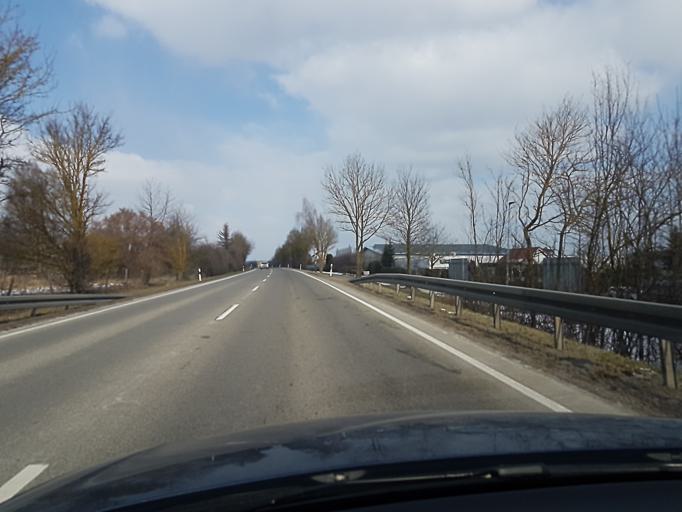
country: DE
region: Baden-Wuerttemberg
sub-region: Regierungsbezirk Stuttgart
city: Bondorf
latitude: 48.5565
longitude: 8.8482
